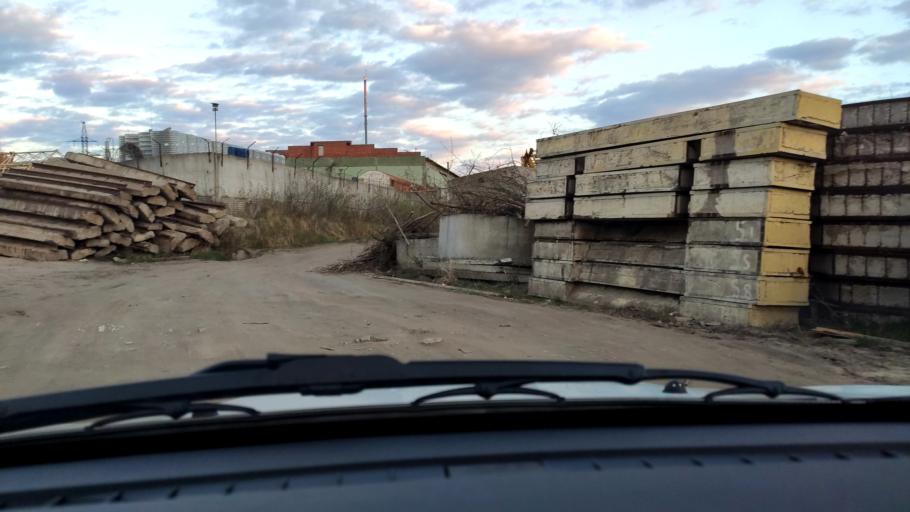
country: RU
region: Voronezj
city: Voronezh
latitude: 51.6870
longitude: 39.1449
